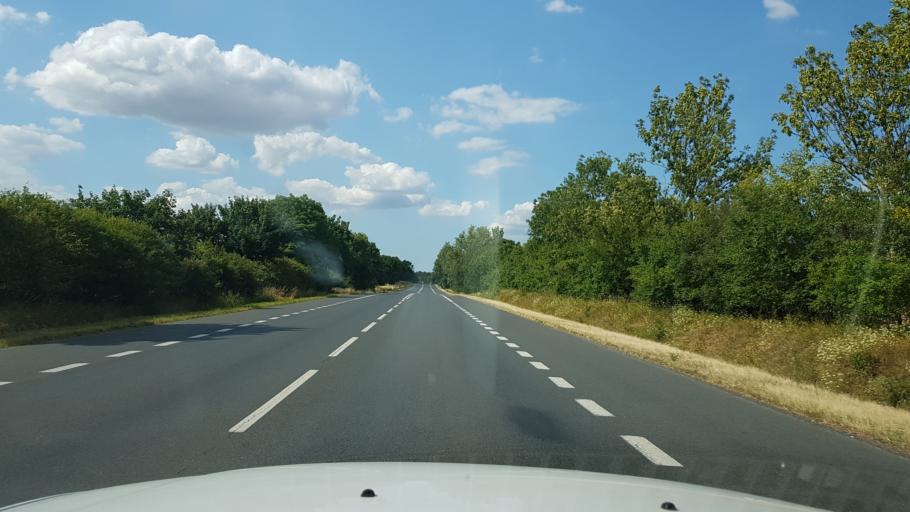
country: PL
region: West Pomeranian Voivodeship
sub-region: Powiat pyrzycki
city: Pyrzyce
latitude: 53.1165
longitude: 14.8931
